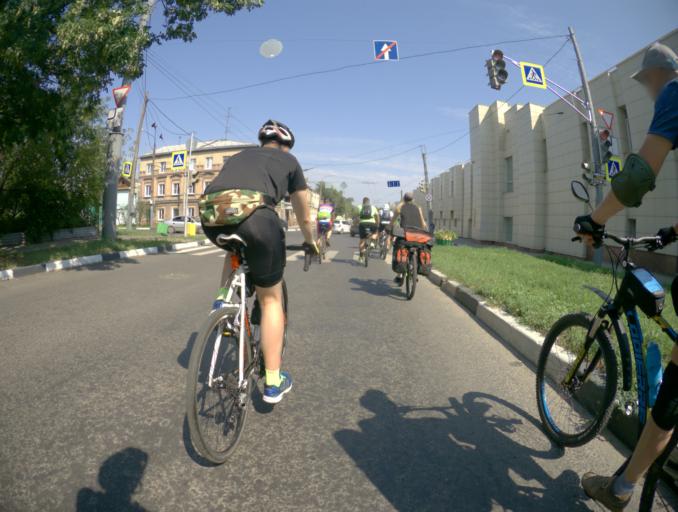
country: RU
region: Nizjnij Novgorod
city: Nizhniy Novgorod
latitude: 56.3180
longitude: 43.9521
